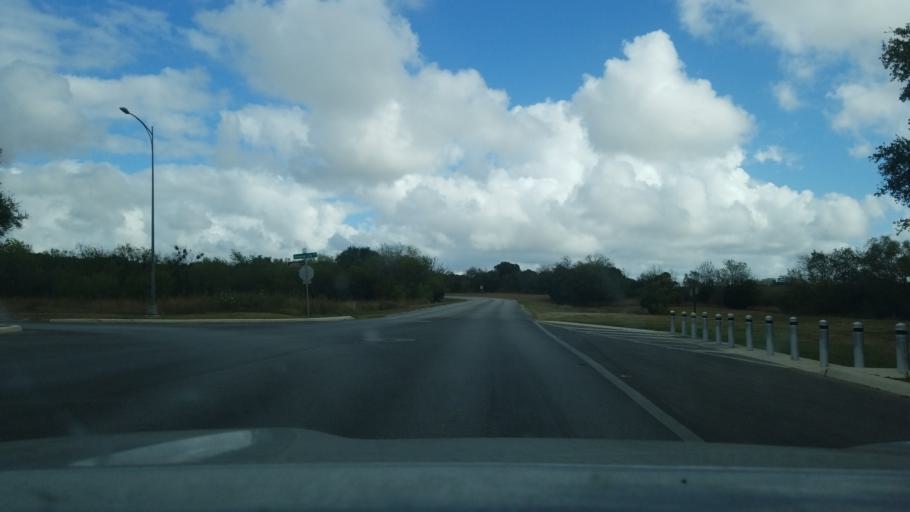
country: US
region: Texas
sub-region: Bexar County
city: Universal City
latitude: 29.5375
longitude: -98.2998
